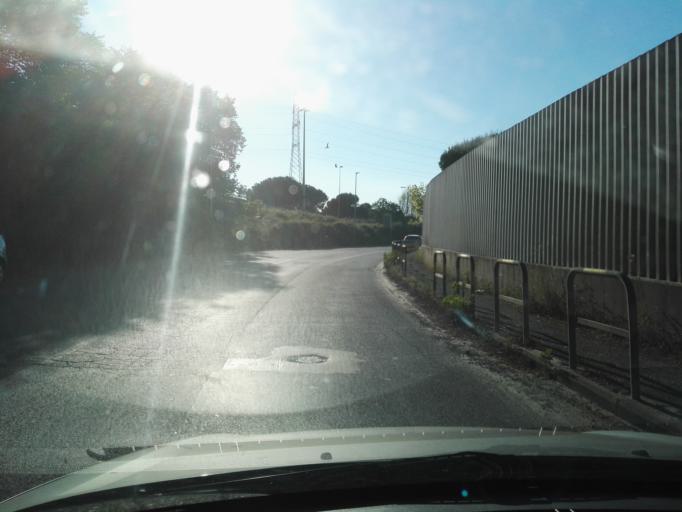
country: IT
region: Latium
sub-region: Citta metropolitana di Roma Capitale
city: Selcetta
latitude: 41.7976
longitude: 12.4837
